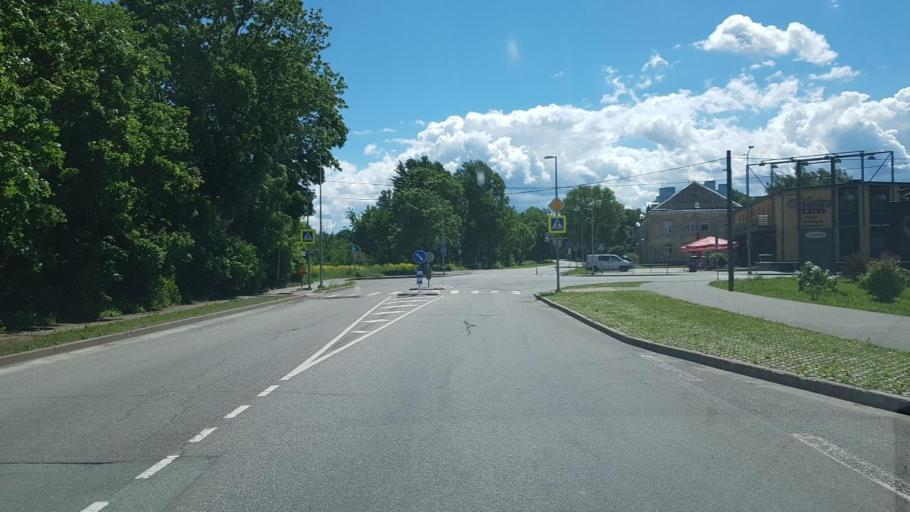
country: EE
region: Ida-Virumaa
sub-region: Narva linn
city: Narva
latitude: 59.3870
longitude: 28.1976
